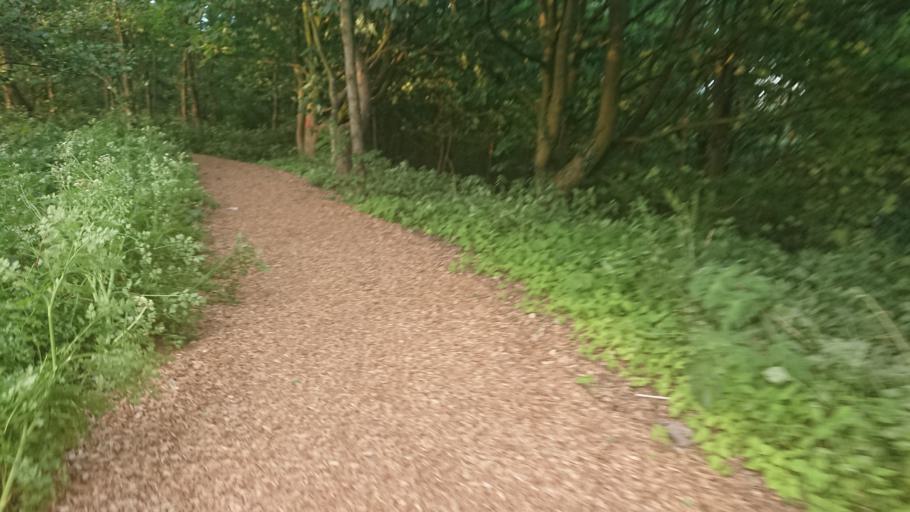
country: GB
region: England
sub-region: Lancashire
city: Galgate
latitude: 53.9993
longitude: -2.7873
